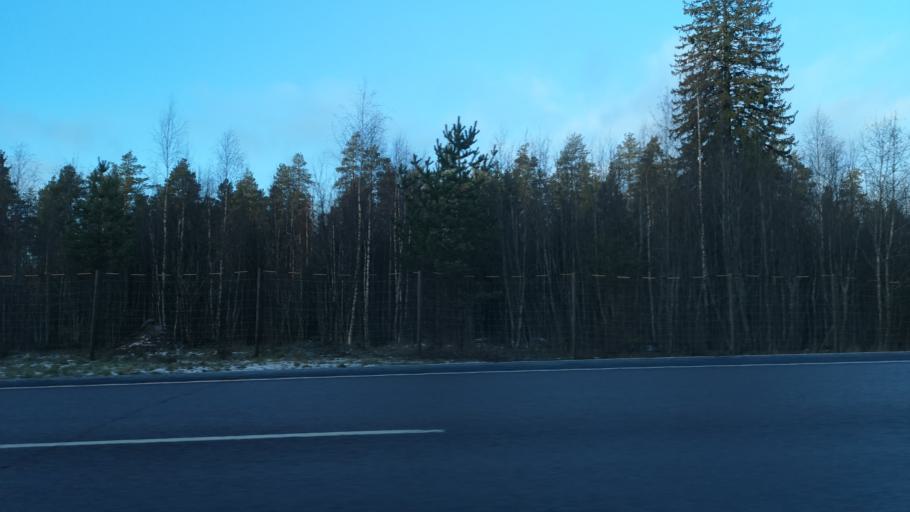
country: FI
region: Paijanne Tavastia
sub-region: Lahti
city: Heinola
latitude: 61.3611
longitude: 26.2412
